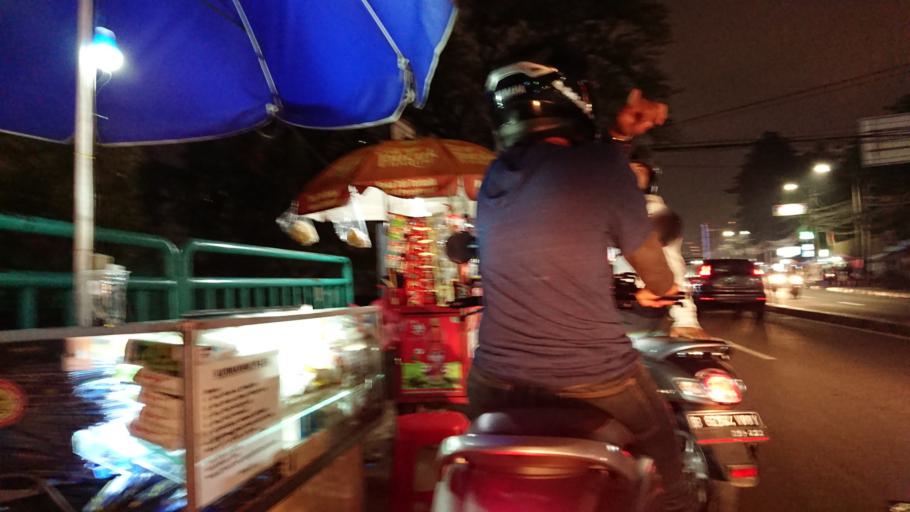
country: ID
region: Jakarta Raya
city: Jakarta
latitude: -6.2003
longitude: 106.8001
